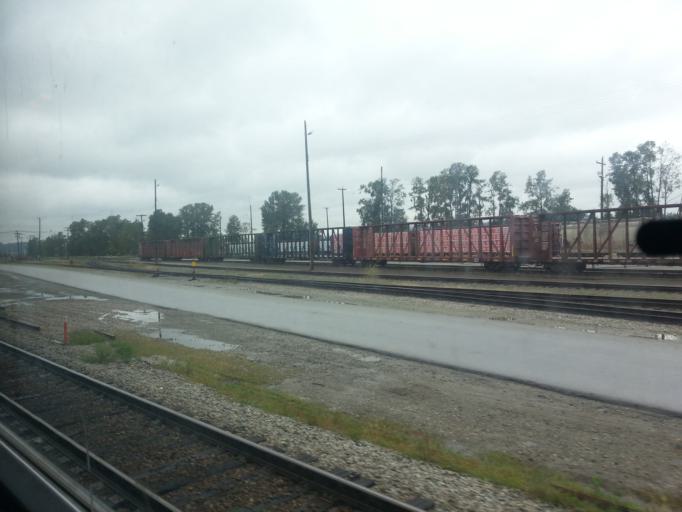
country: CA
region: British Columbia
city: Port Moody
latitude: 49.2155
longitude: -122.8359
